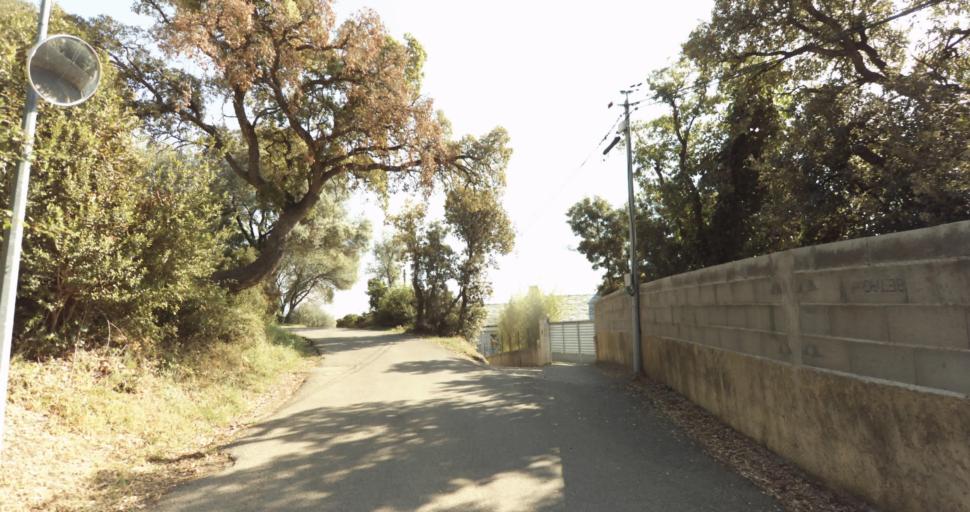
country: FR
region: Corsica
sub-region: Departement de la Haute-Corse
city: Biguglia
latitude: 42.6312
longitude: 9.4179
